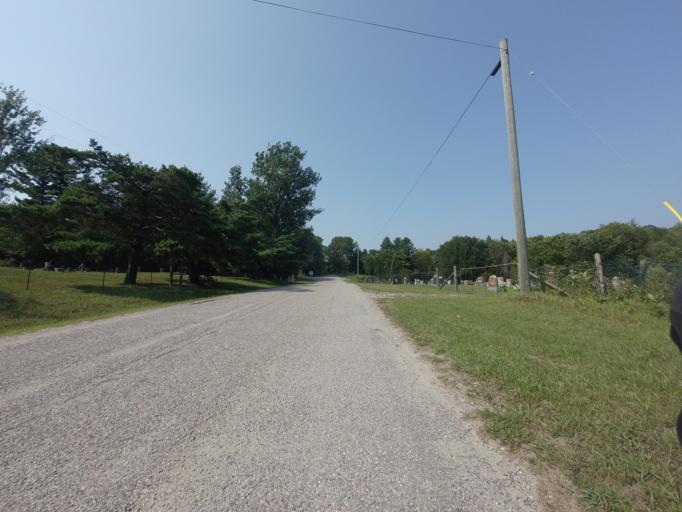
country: CA
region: Ontario
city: Skatepark
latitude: 44.7415
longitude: -76.8279
